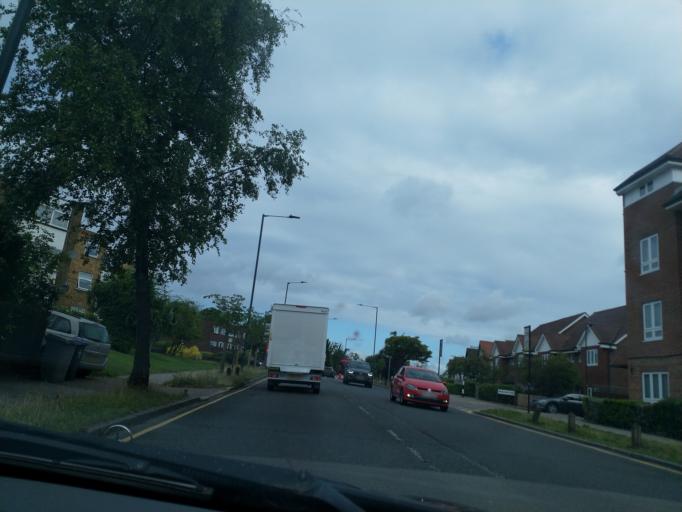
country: GB
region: England
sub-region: Greater London
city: Harrow on the Hill
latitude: 51.5626
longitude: -0.3203
